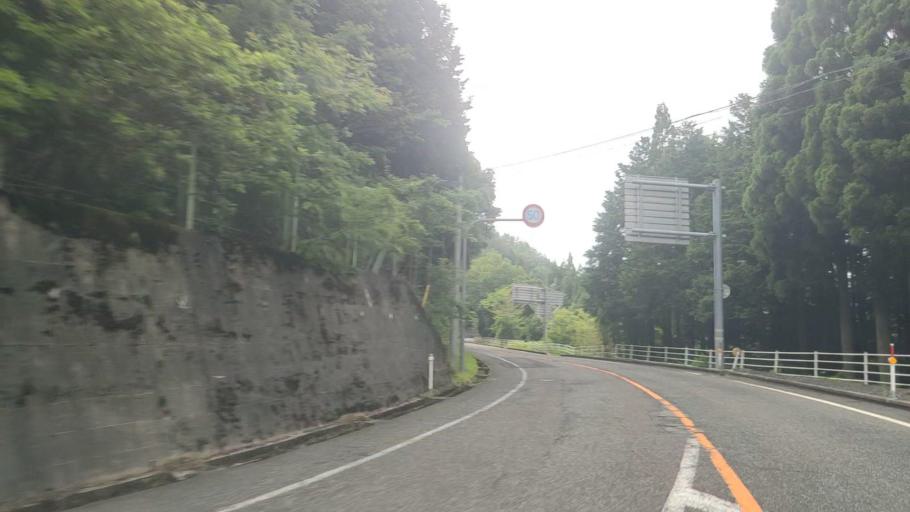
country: JP
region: Tottori
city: Kurayoshi
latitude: 35.2919
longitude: 133.9456
